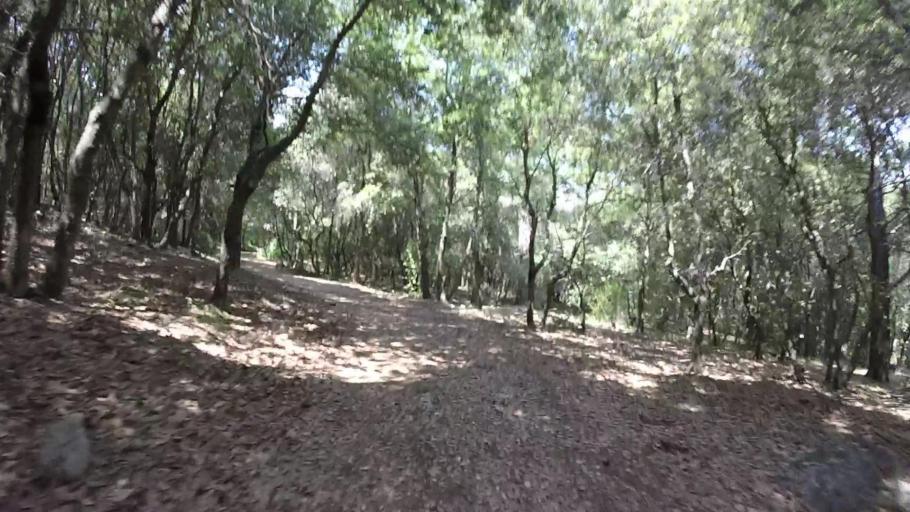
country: FR
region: Provence-Alpes-Cote d'Azur
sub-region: Departement des Alpes-Maritimes
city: Valbonne
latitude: 43.6272
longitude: 7.0305
